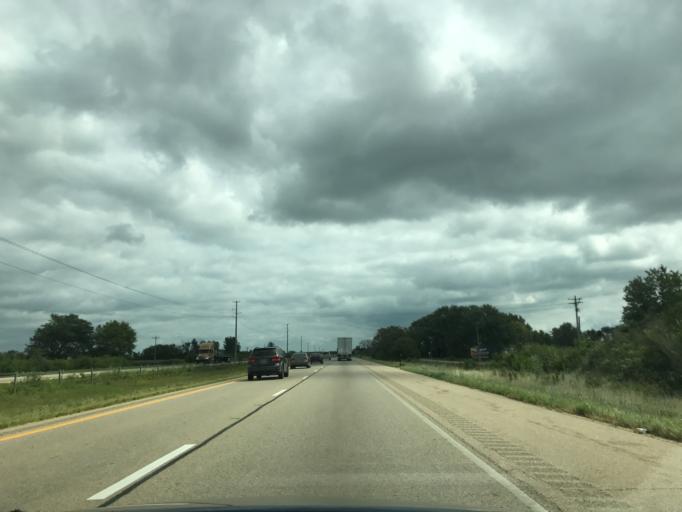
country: US
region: Illinois
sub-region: LaSalle County
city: Ottawa
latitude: 41.3684
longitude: -88.8835
